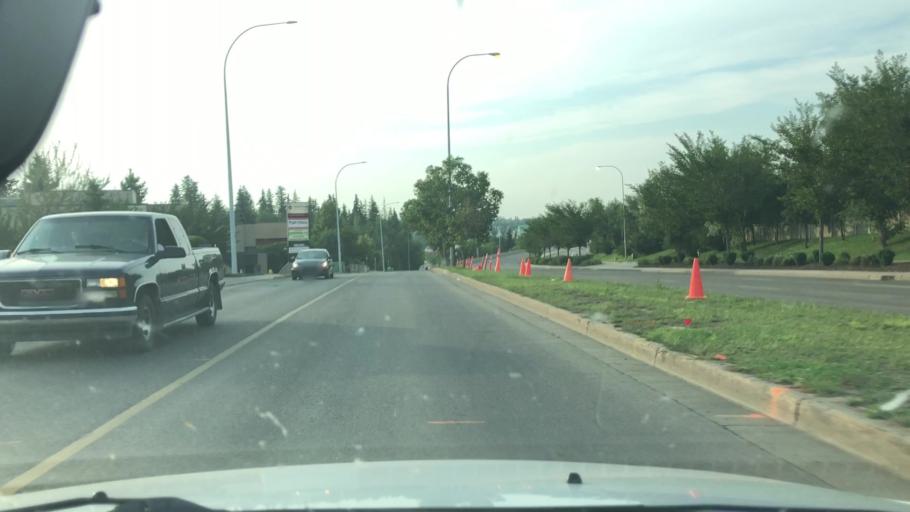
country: CA
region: Alberta
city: St. Albert
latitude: 53.6288
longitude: -113.6204
